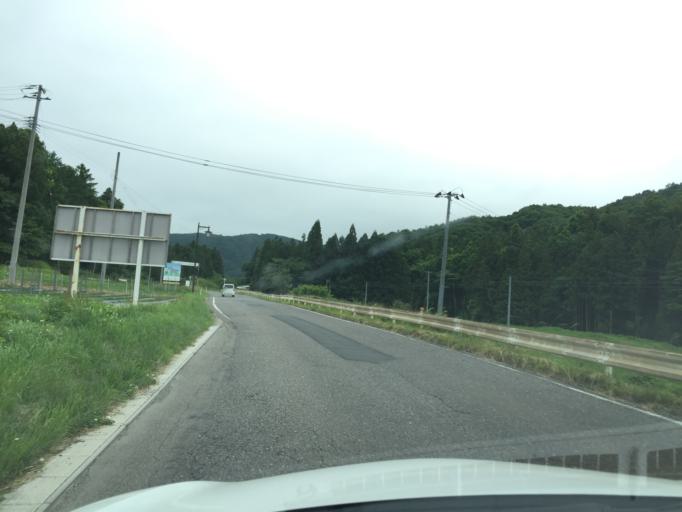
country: JP
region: Fukushima
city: Funehikimachi-funehiki
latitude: 37.3663
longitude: 140.6385
